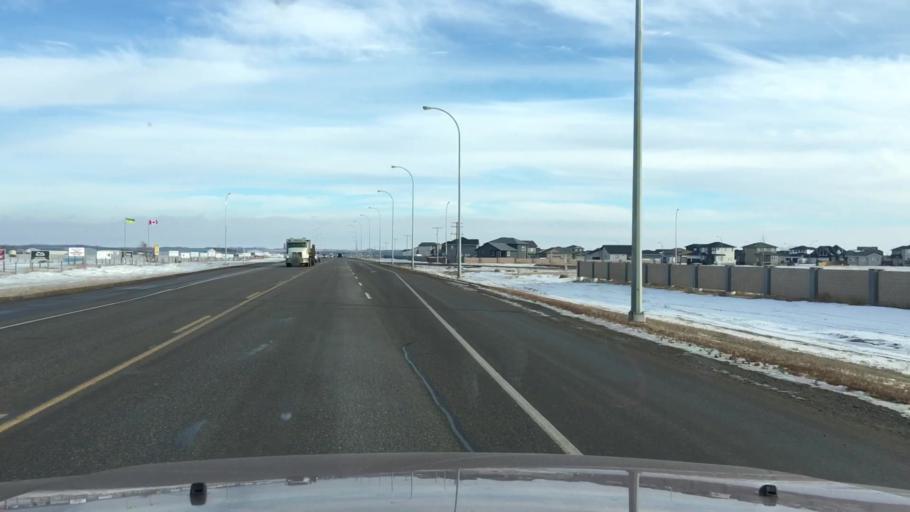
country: CA
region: Saskatchewan
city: Pilot Butte
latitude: 50.4872
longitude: -104.4226
